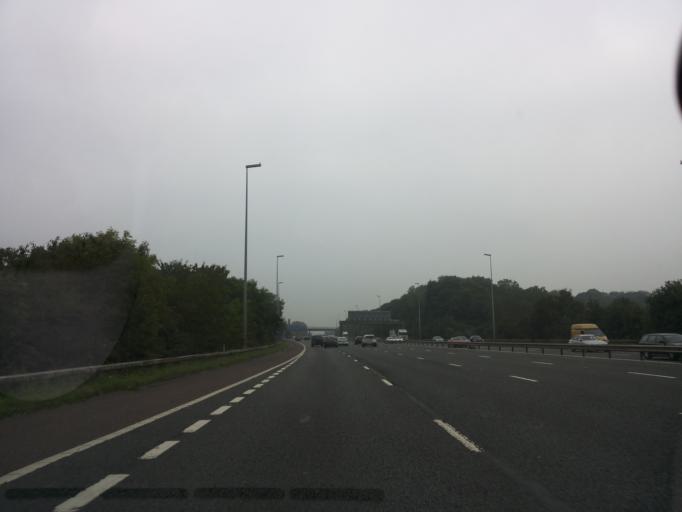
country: GB
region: England
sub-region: Lancashire
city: Goosnargh
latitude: 53.7729
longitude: -2.6404
